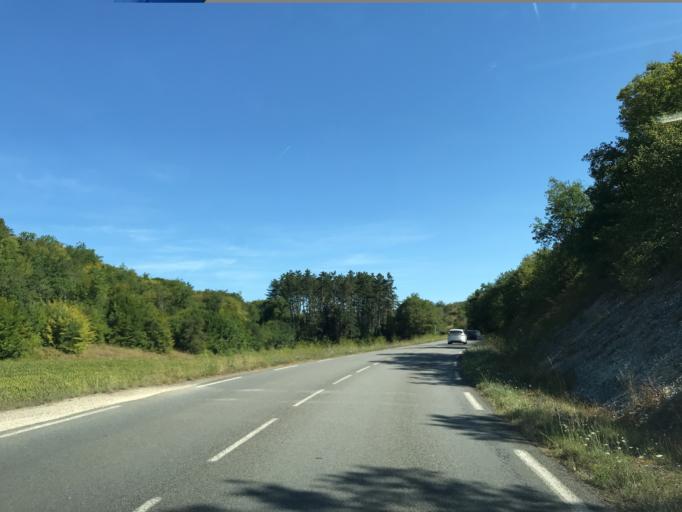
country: FR
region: Limousin
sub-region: Departement de la Correze
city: Larche
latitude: 45.0338
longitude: 1.3742
